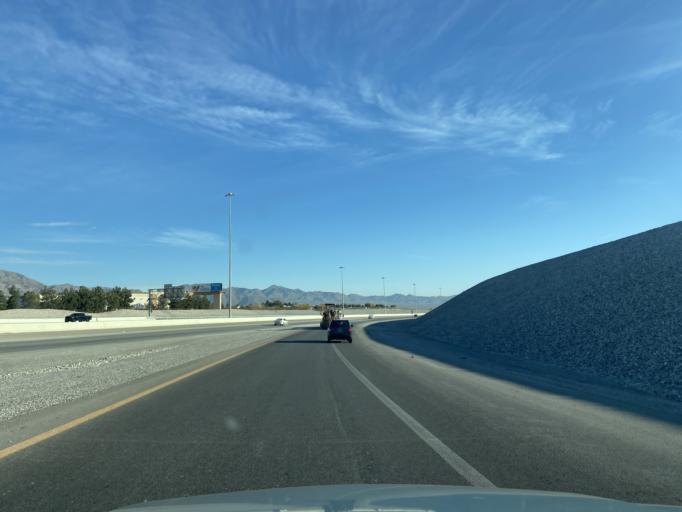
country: US
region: Nevada
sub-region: Clark County
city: North Las Vegas
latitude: 36.2912
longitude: -115.1769
